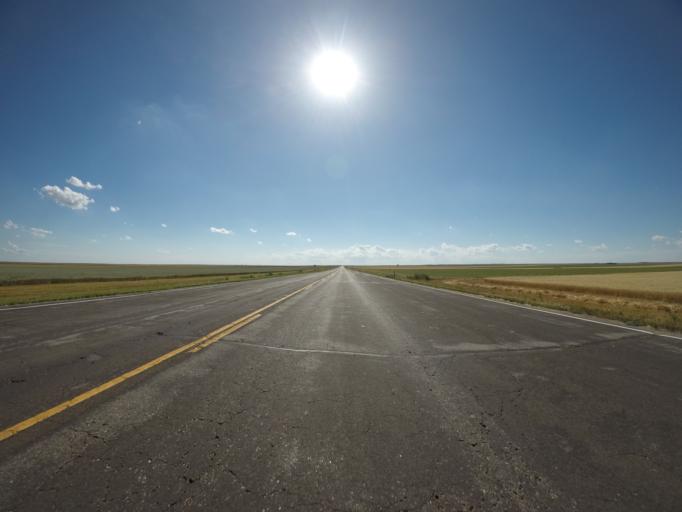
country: US
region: Colorado
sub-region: Logan County
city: Sterling
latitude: 40.6240
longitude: -103.3558
